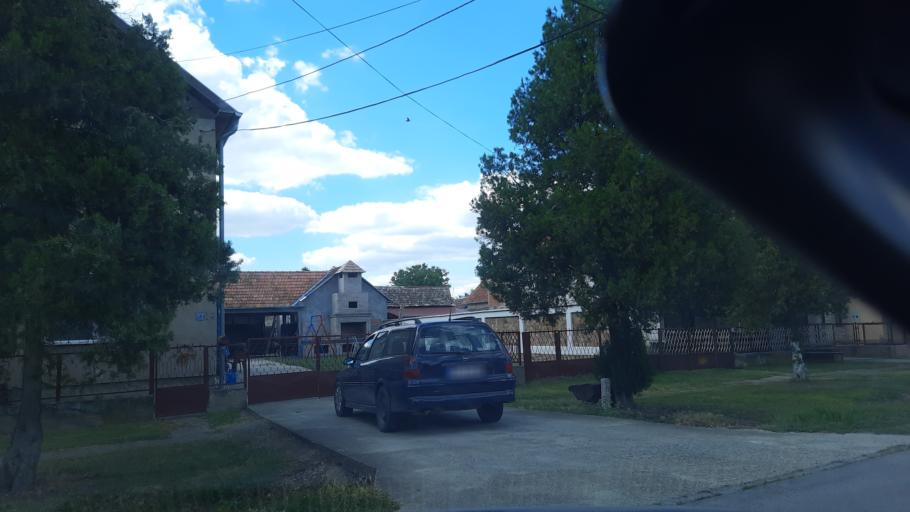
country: RS
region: Autonomna Pokrajina Vojvodina
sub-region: Sremski Okrug
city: Pecinci
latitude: 44.9158
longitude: 19.9685
